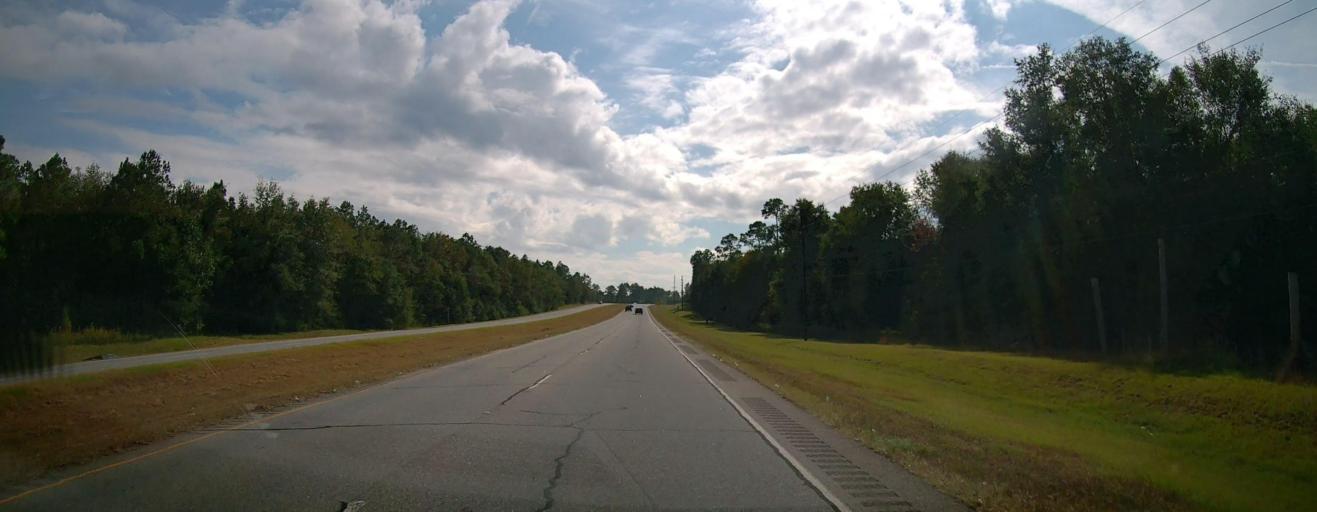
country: US
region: Georgia
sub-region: Mitchell County
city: Camilla
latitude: 31.3215
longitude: -84.1736
